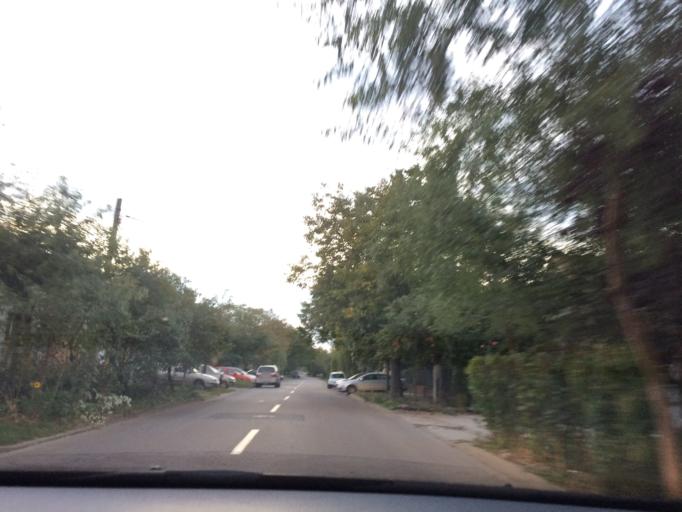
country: RO
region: Timis
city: Timisoara
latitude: 45.7626
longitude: 21.1990
